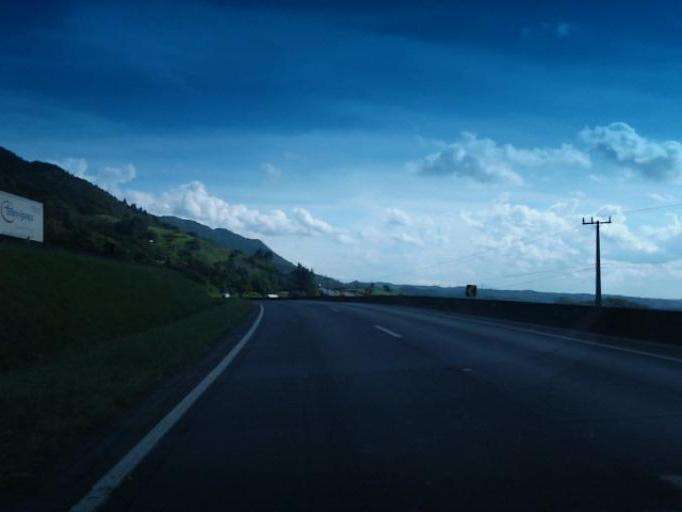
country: BR
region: Parana
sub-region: Campina Grande Do Sul
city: Campina Grande do Sul
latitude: -25.1483
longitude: -48.8592
